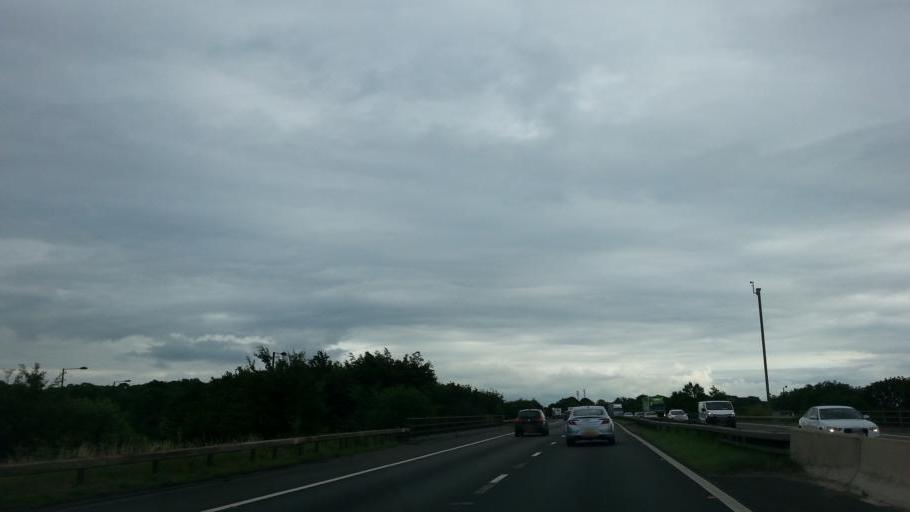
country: GB
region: England
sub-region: Doncaster
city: Marr
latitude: 53.5431
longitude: -1.2075
